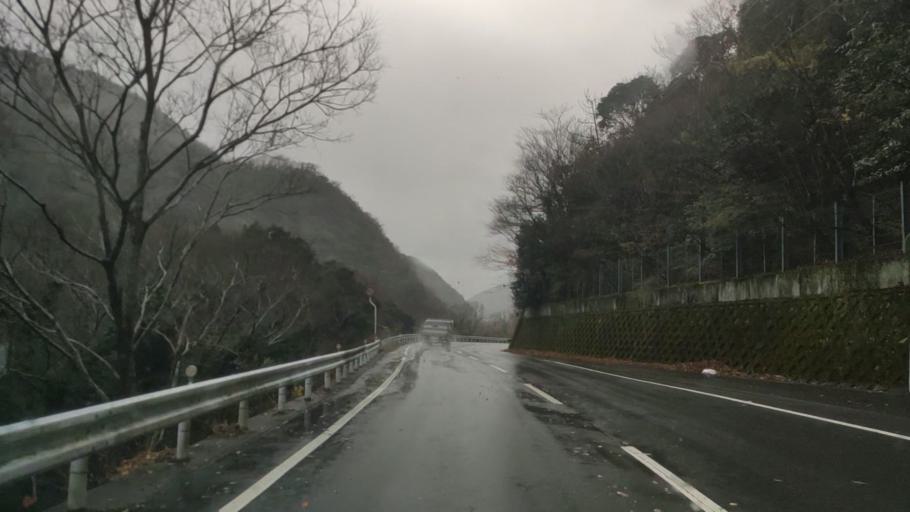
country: JP
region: Tokushima
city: Kamojimacho-jogejima
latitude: 34.1452
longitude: 134.3540
